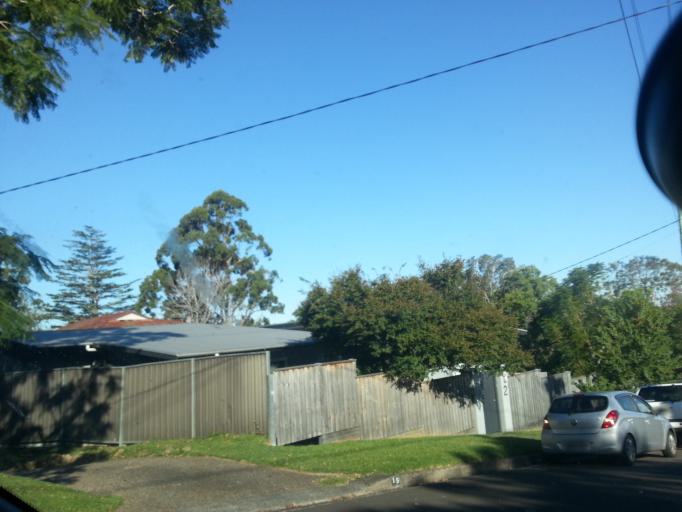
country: AU
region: New South Wales
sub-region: Wollongong
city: Mount Keira
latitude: -34.4148
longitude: 150.8572
